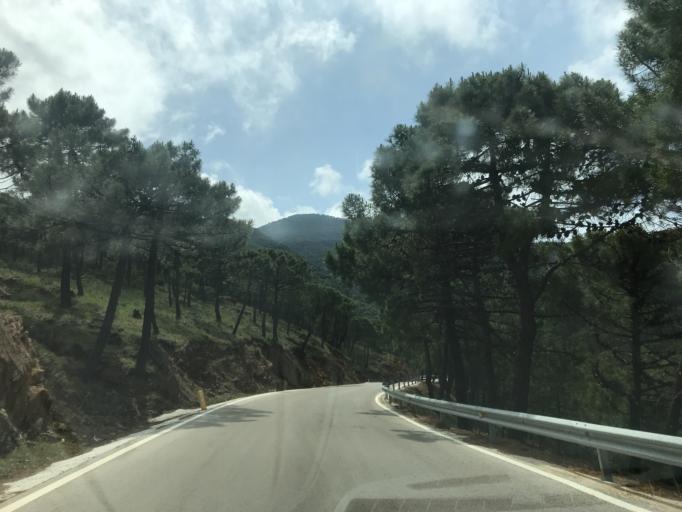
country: ES
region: Andalusia
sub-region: Provincia de Malaga
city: Estepona
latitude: 36.4896
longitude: -5.1815
